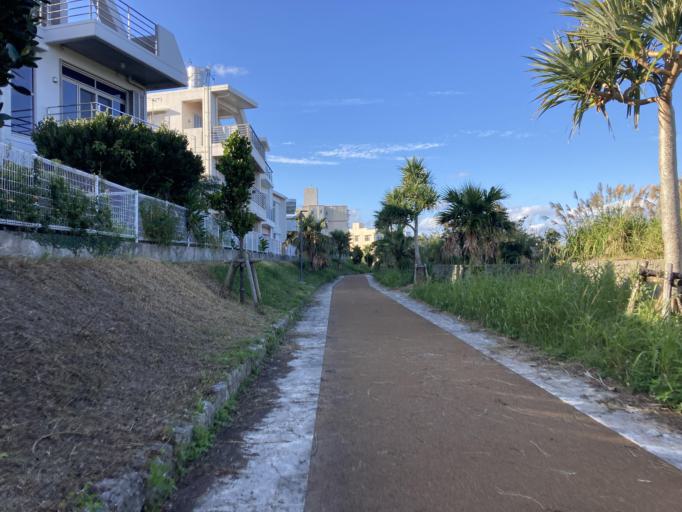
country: JP
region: Okinawa
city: Ginowan
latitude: 26.2564
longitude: 127.7777
